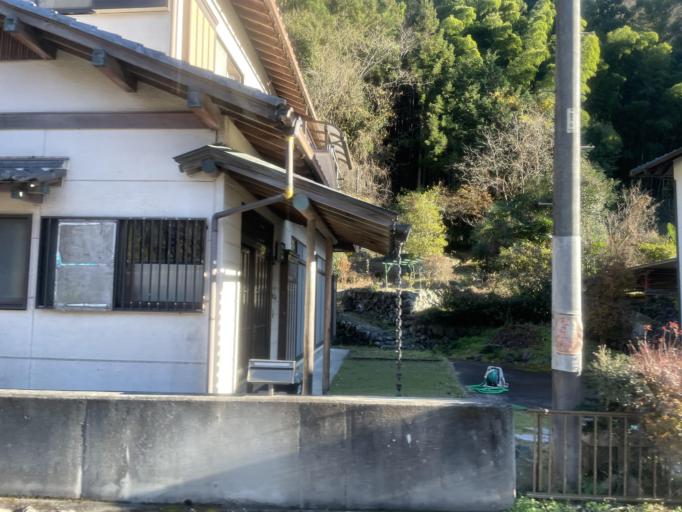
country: JP
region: Saitama
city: Yorii
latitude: 36.0622
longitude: 139.1814
